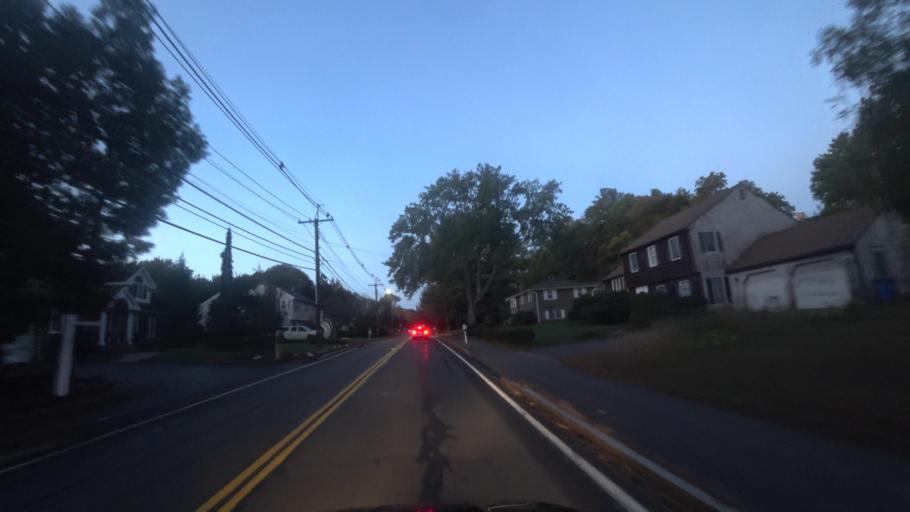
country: US
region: Massachusetts
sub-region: Middlesex County
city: Wakefield
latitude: 42.5022
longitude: -71.0473
